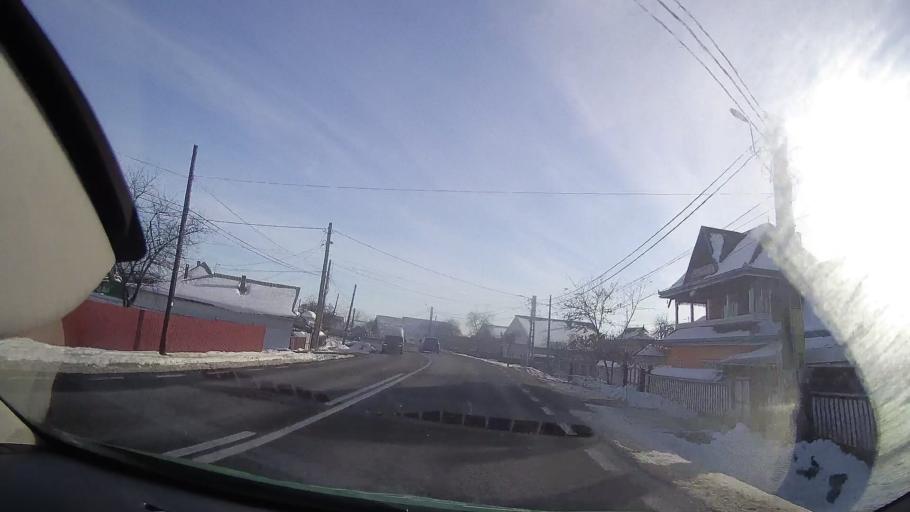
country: RO
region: Neamt
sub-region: Comuna Cracaoani
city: Cracaoani
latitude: 47.0898
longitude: 26.3244
